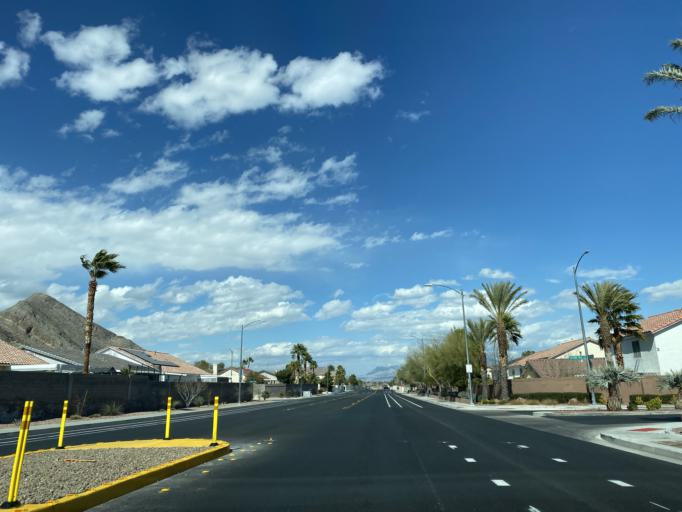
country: US
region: Nevada
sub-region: Clark County
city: Summerlin South
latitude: 36.2279
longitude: -115.3064
